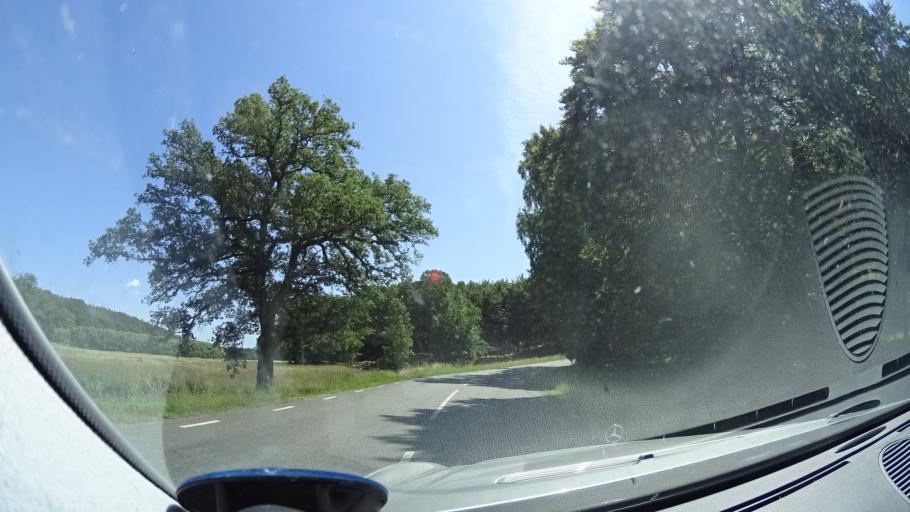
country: SE
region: Skane
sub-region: Kristianstads Kommun
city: Degeberga
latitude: 55.8958
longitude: 14.0024
